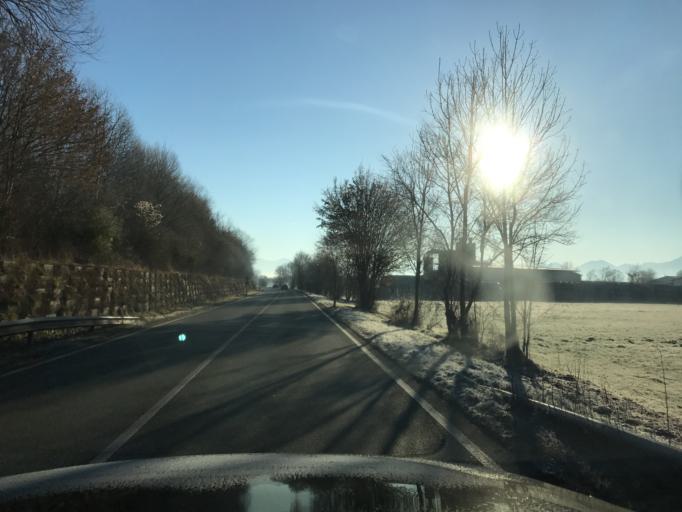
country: DE
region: Bavaria
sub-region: Upper Bavaria
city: Bad Aibling
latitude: 47.8552
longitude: 11.9944
